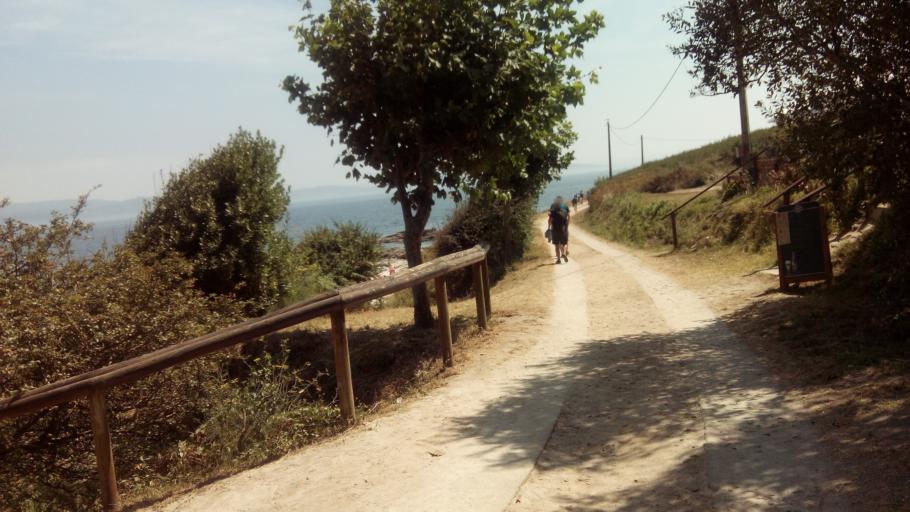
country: ES
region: Galicia
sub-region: Provincia de Pontevedra
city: Sanxenxo
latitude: 42.3740
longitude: -8.9333
